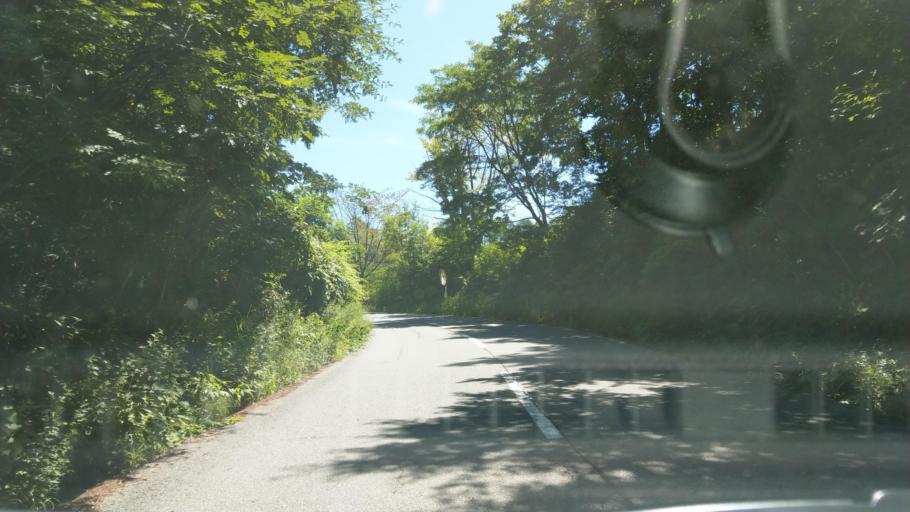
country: JP
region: Nagano
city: Komoro
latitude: 36.3853
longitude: 138.4636
